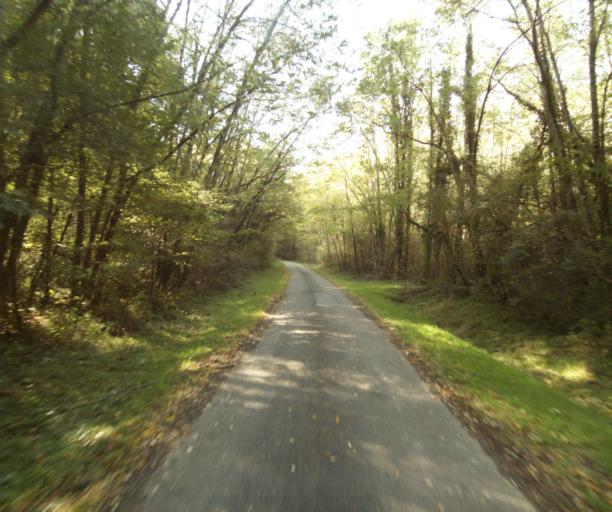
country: FR
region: Midi-Pyrenees
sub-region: Departement du Tarn-et-Garonne
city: Nohic
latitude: 43.9275
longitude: 1.4453
